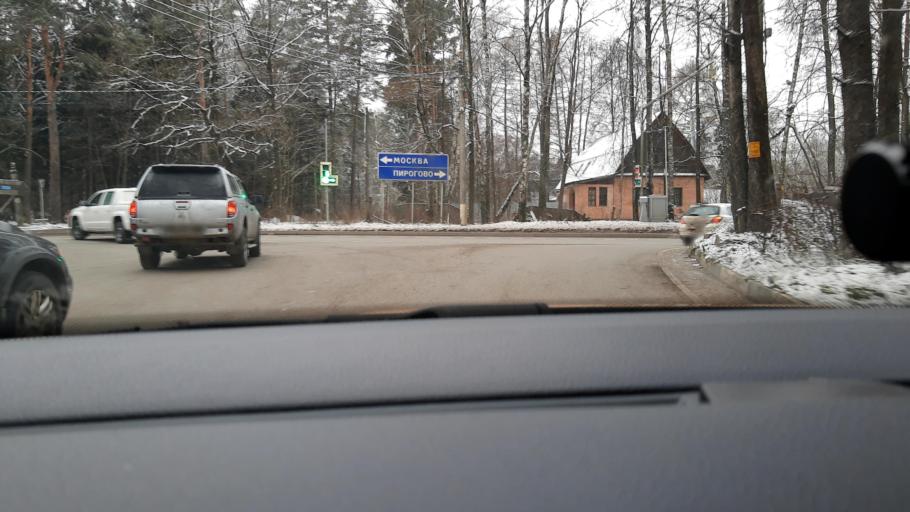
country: RU
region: Moskovskaya
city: Pirogovskiy
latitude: 55.9449
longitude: 37.7527
